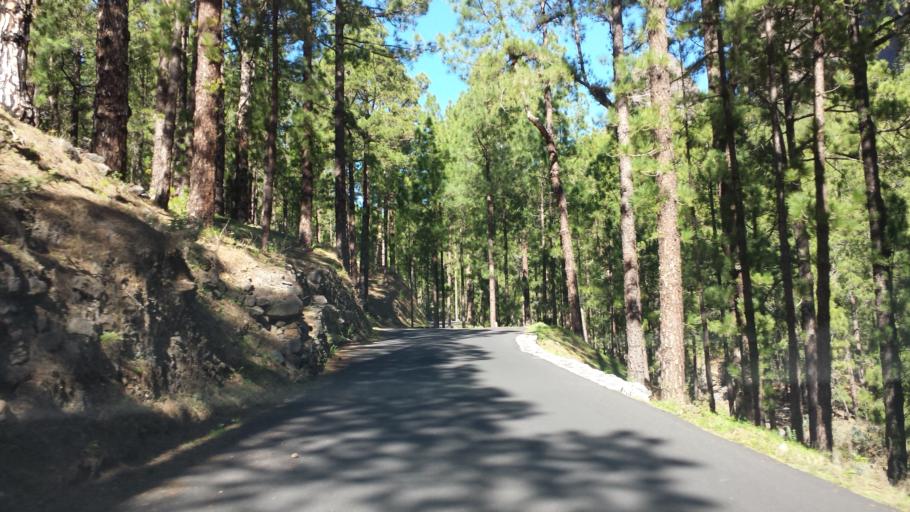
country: ES
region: Canary Islands
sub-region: Provincia de Santa Cruz de Tenerife
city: El Paso
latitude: 28.6916
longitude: -17.8517
